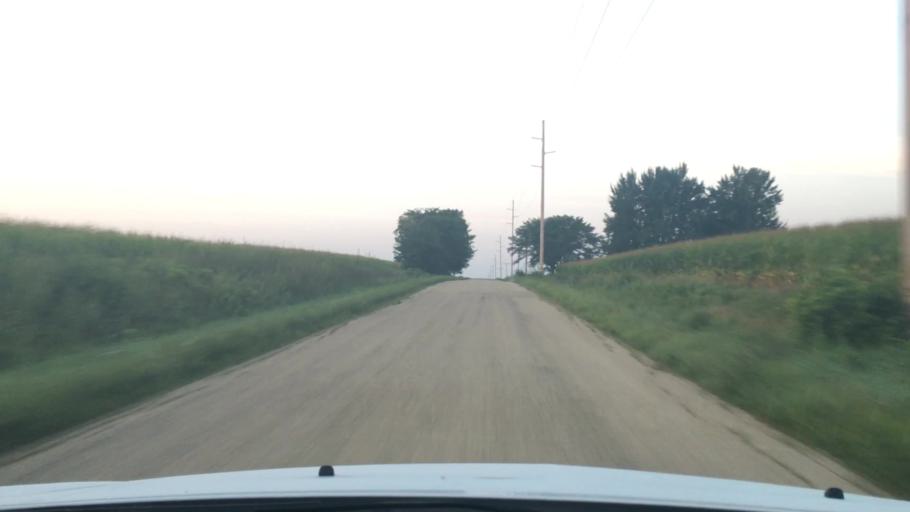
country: US
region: Illinois
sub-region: Ogle County
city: Rochelle
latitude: 41.8641
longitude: -89.0007
